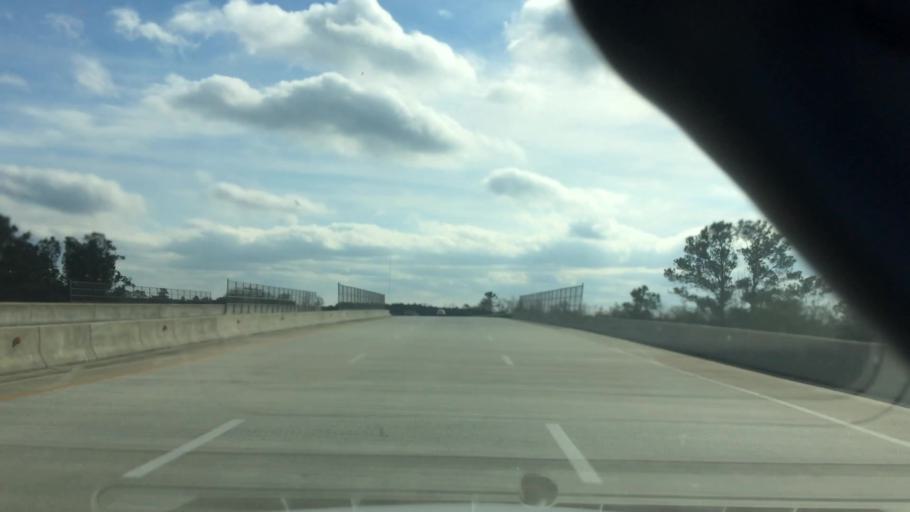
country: US
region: North Carolina
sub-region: Brunswick County
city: Leland
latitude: 34.2582
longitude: -78.0801
